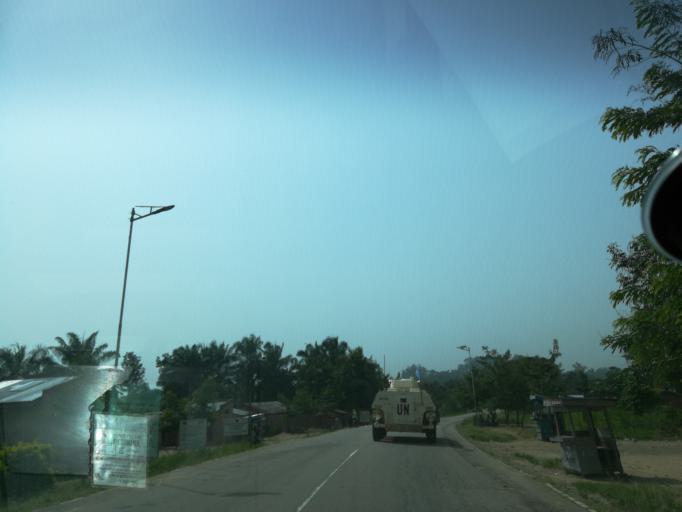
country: CD
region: Nord Kivu
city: Beni
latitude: 0.5418
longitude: 29.4903
